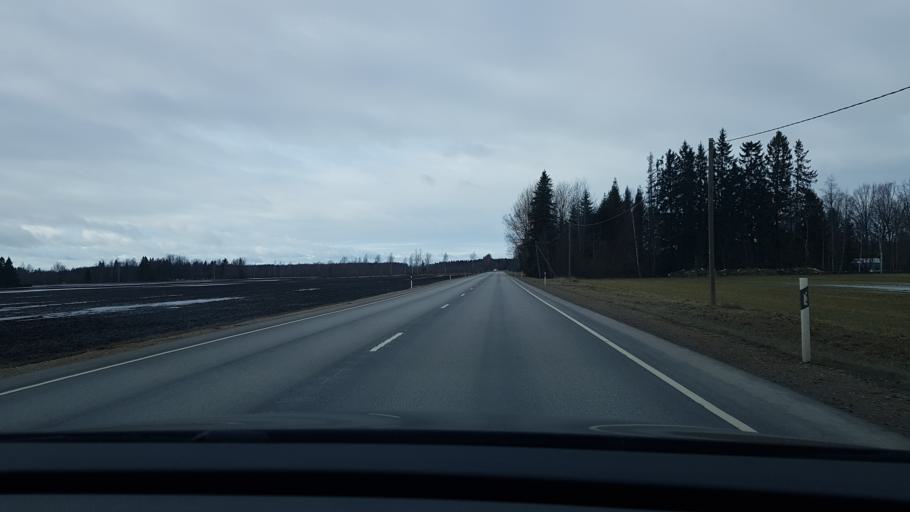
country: EE
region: Paernumaa
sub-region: Paikuse vald
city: Paikuse
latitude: 58.2629
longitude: 24.6616
